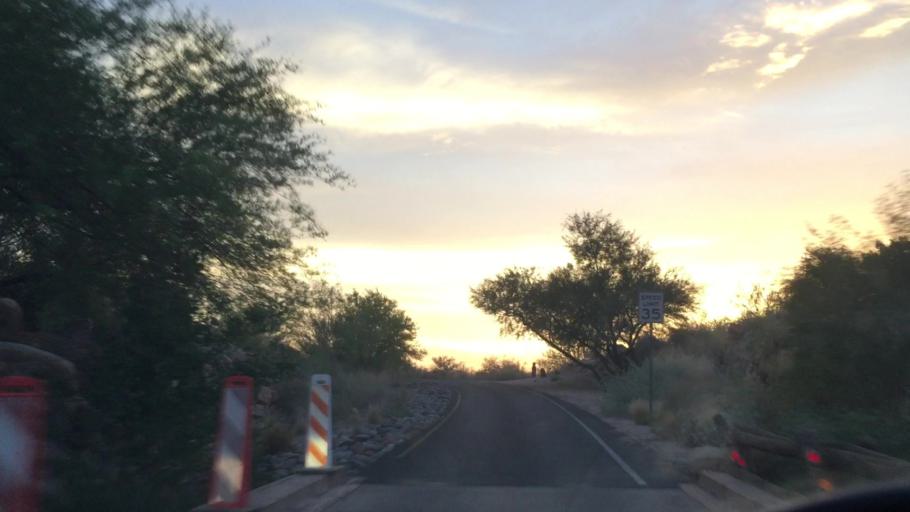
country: US
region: Arizona
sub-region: Maricopa County
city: Guadalupe
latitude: 33.2766
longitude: -111.9794
